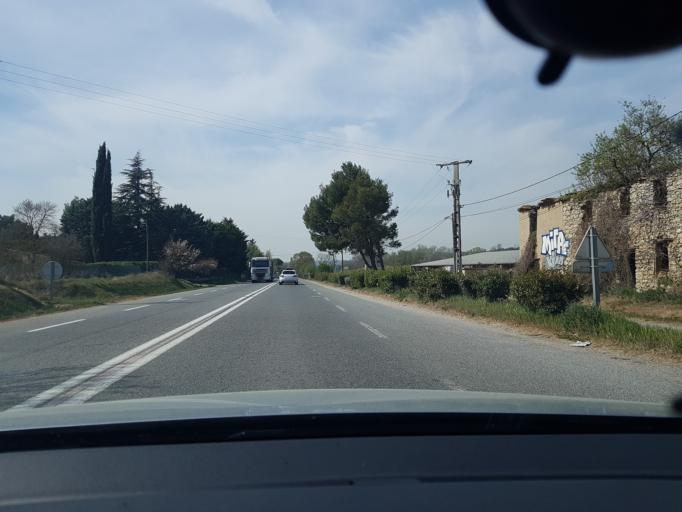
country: FR
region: Provence-Alpes-Cote d'Azur
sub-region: Departement des Bouches-du-Rhone
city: Chateauneuf-le-Rouge
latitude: 43.4718
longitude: 5.5840
